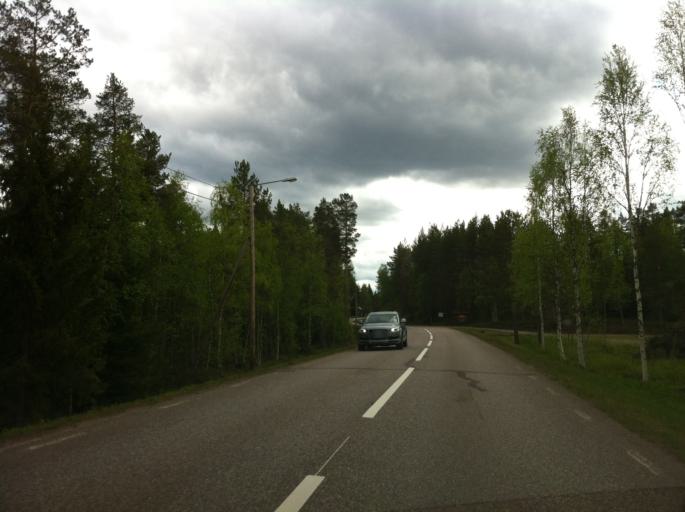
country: NO
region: Hedmark
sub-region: Trysil
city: Innbygda
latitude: 61.4177
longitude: 13.0860
